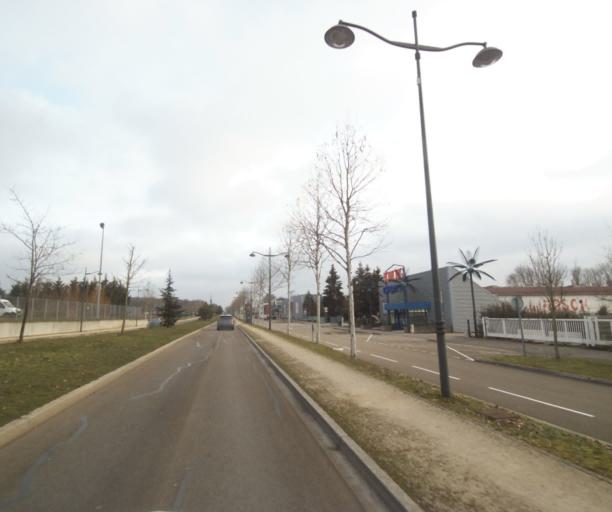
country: FR
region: Champagne-Ardenne
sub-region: Departement de la Haute-Marne
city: Bettancourt-la-Ferree
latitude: 48.6532
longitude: 4.9643
